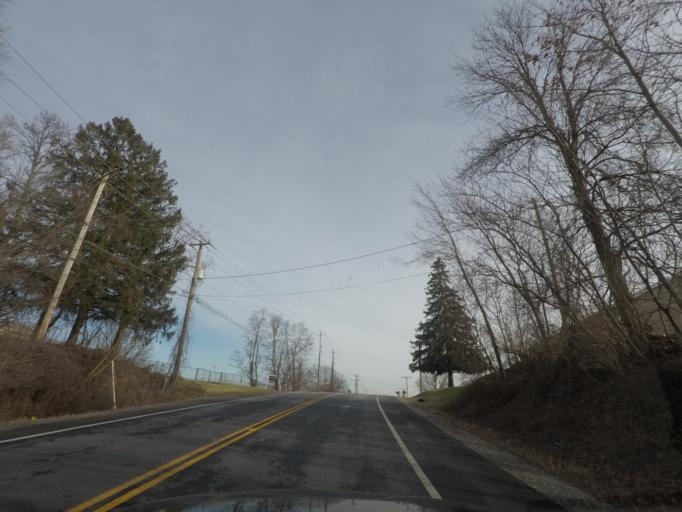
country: US
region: New York
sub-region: Saratoga County
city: Mechanicville
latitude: 42.8716
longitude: -73.7240
